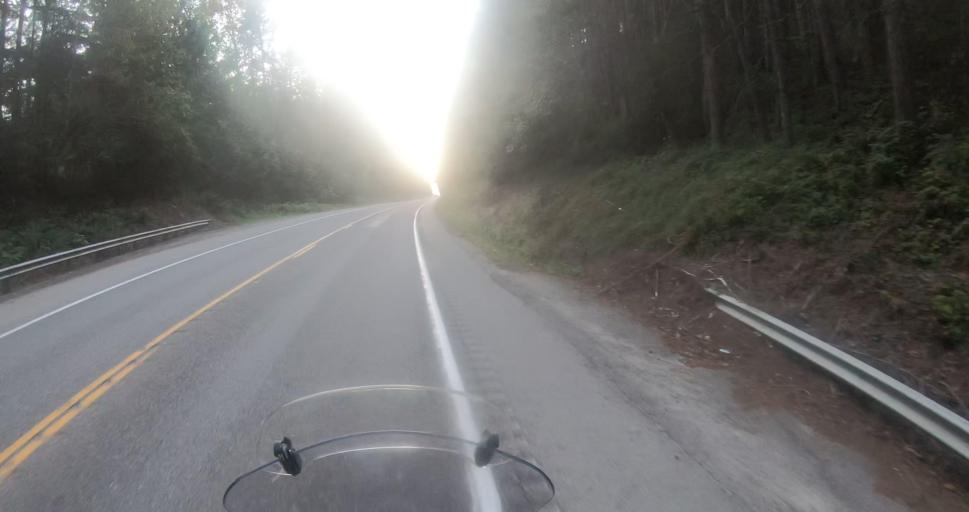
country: US
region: Washington
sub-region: Lewis County
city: Morton
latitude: 46.5375
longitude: -122.0170
